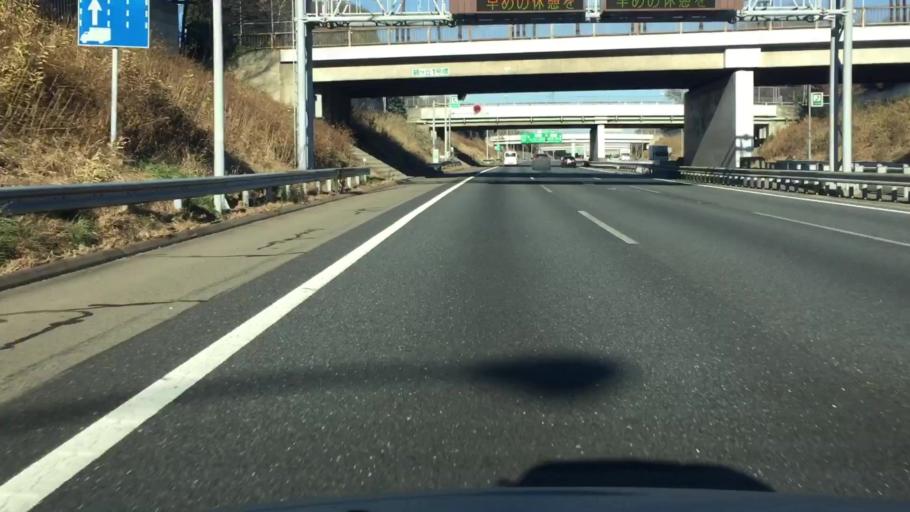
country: JP
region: Saitama
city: Sakado
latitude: 35.9234
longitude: 139.4127
